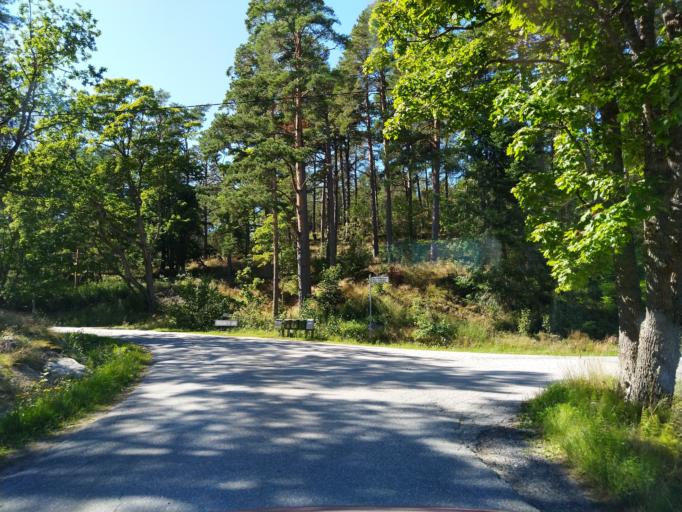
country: FI
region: Varsinais-Suomi
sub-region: Aboland-Turunmaa
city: Dragsfjaerd
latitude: 60.0359
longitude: 22.4330
